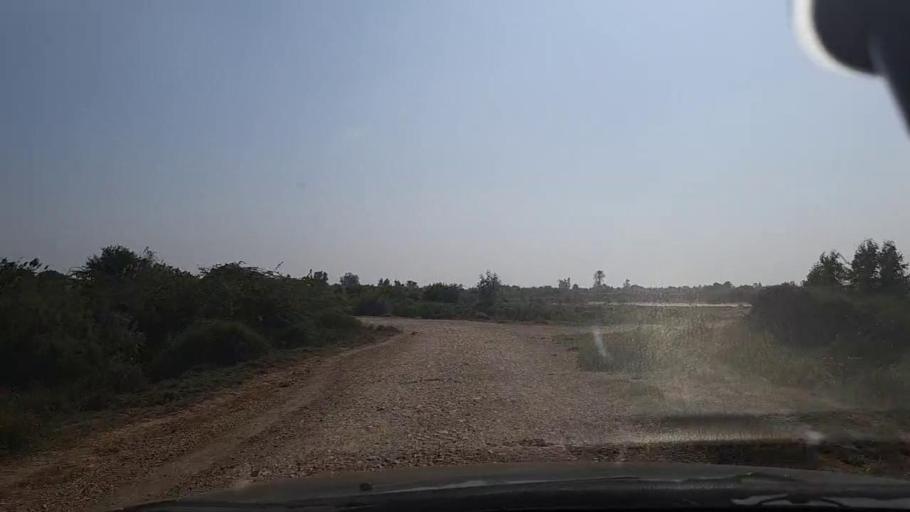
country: PK
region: Sindh
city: Chuhar Jamali
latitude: 24.5178
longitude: 67.8838
